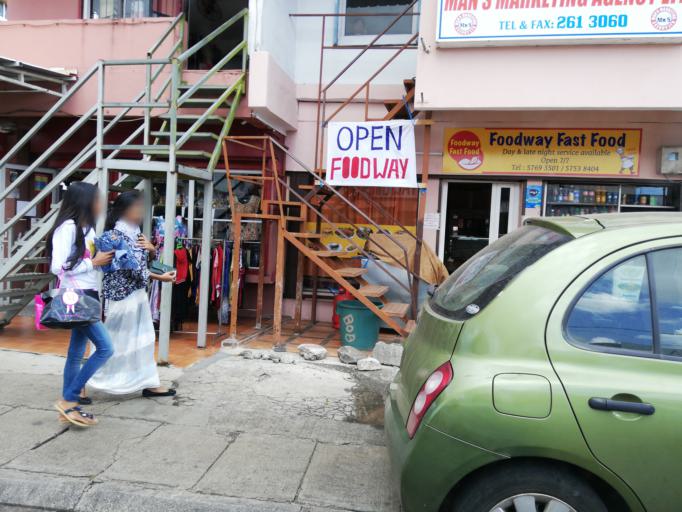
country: MU
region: Pamplemousses
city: Triolet
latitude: -20.0577
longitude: 57.5522
